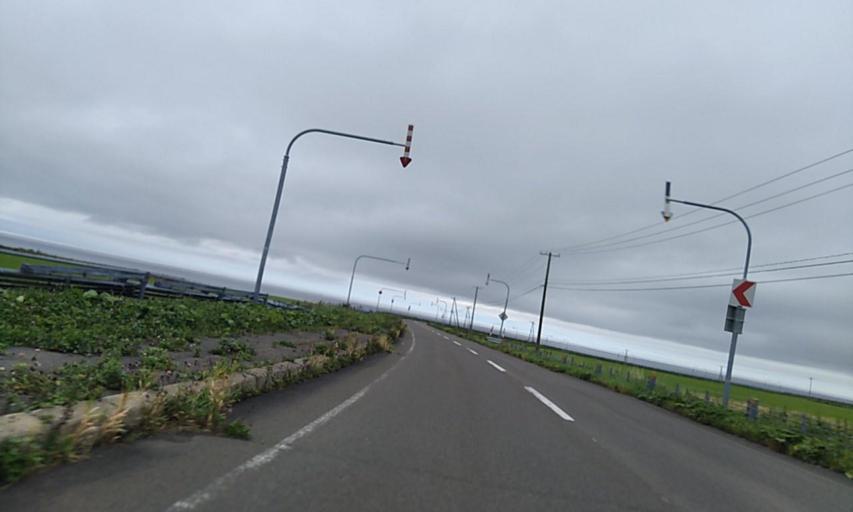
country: JP
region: Hokkaido
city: Nemuro
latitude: 43.3767
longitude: 145.6449
